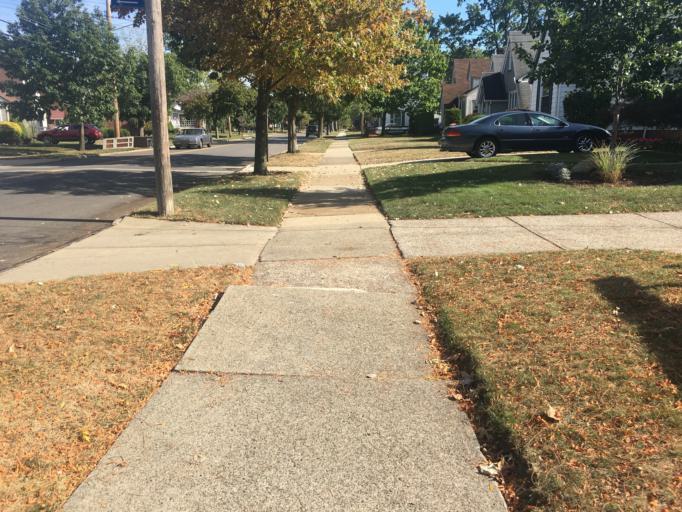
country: US
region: Ohio
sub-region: Cuyahoga County
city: Lakewood
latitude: 41.4615
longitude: -81.8115
